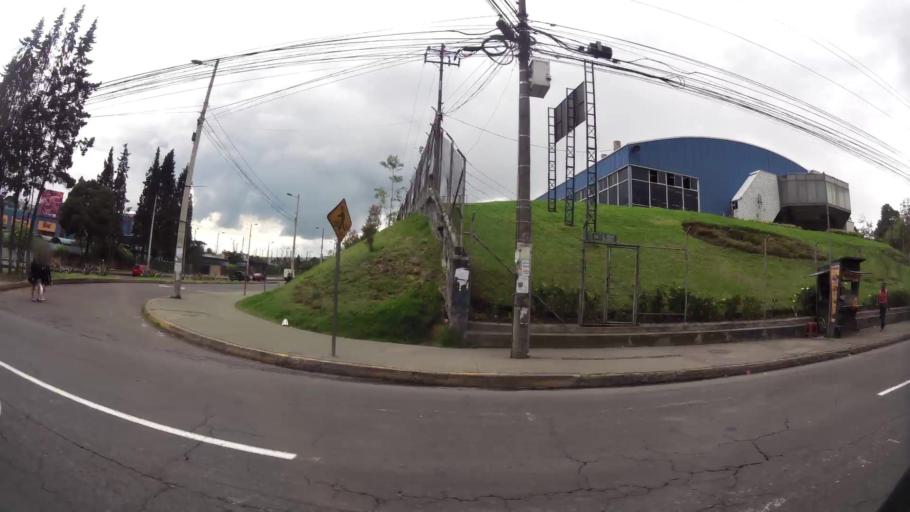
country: EC
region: Pichincha
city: Quito
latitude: -0.2827
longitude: -78.5445
